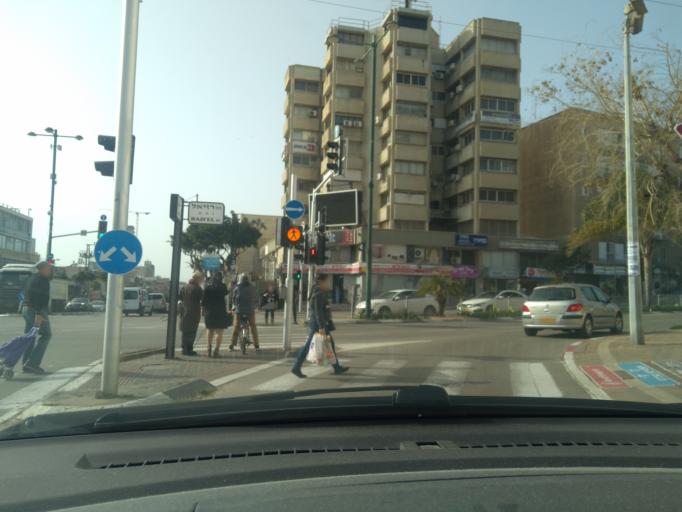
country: IL
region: Central District
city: Netanya
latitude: 32.3271
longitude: 34.8618
